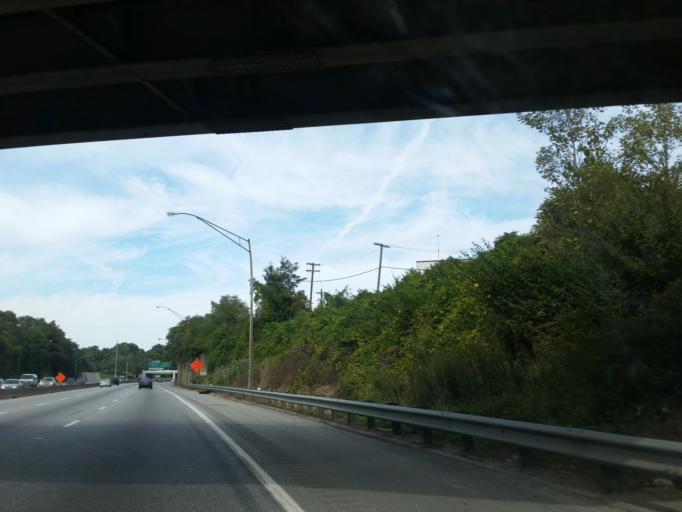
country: US
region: Ohio
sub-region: Cuyahoga County
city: Newburgh Heights
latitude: 41.4441
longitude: -81.6521
